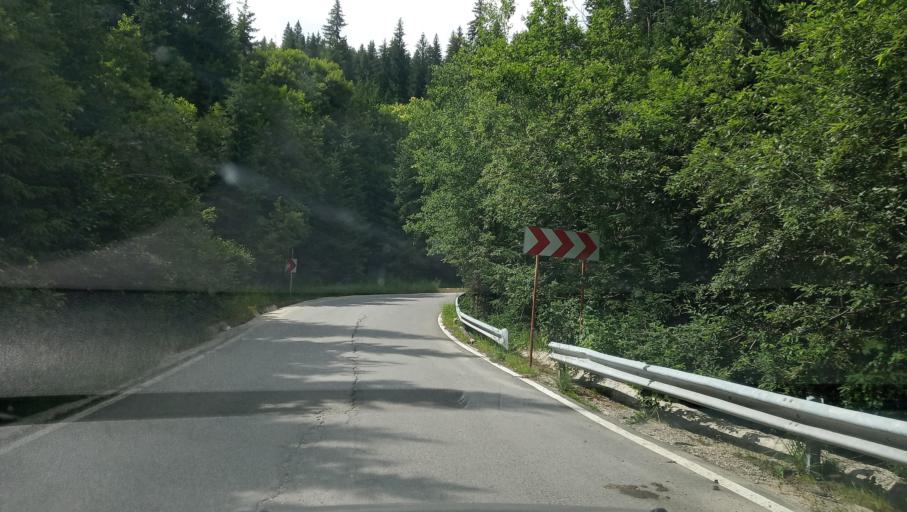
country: RO
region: Dambovita
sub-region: Comuna Moroeni
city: Glod
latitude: 45.3400
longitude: 25.4251
